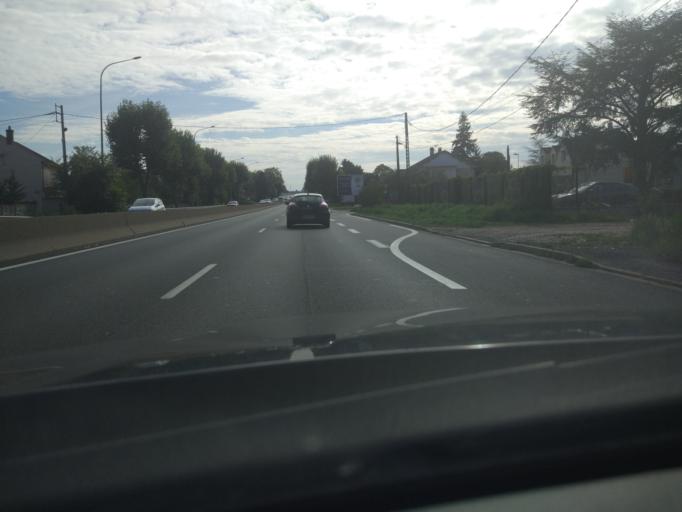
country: FR
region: Ile-de-France
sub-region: Departement de l'Essonne
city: Leuville-sur-Orge
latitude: 48.6088
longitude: 2.2517
